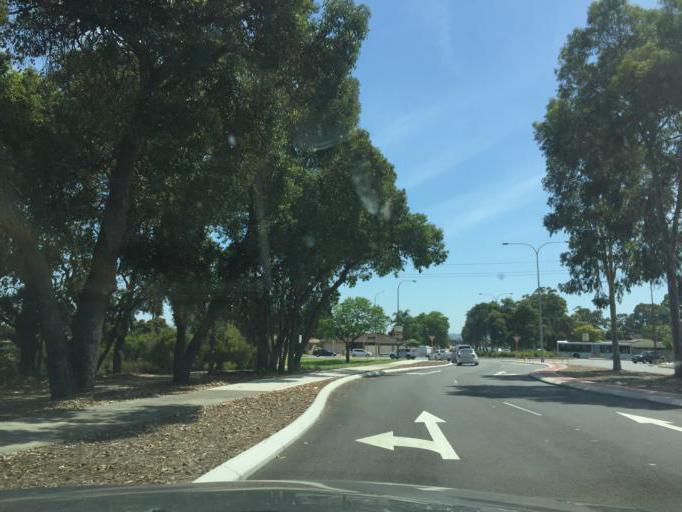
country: AU
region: Western Australia
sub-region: Gosnells
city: Thornlie
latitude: -32.0758
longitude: 115.9604
